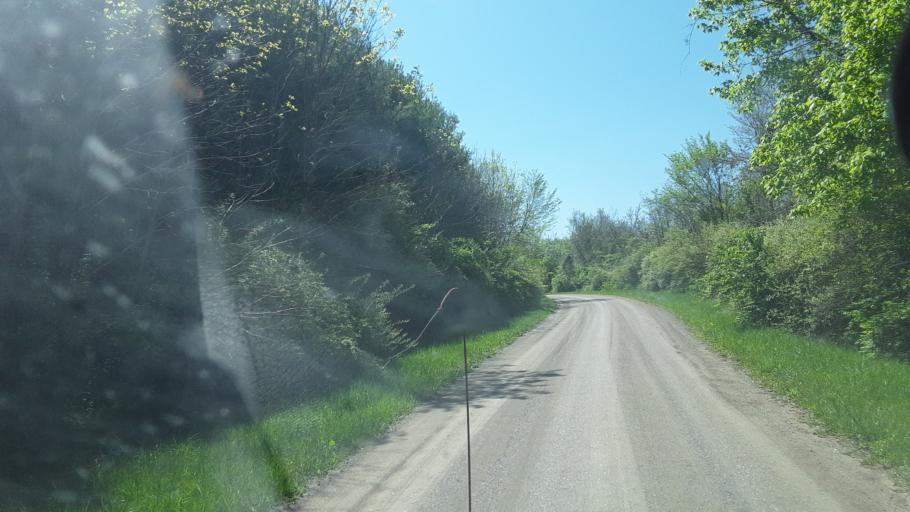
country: US
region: Ohio
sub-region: Noble County
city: Caldwell
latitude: 39.7773
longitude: -81.6189
